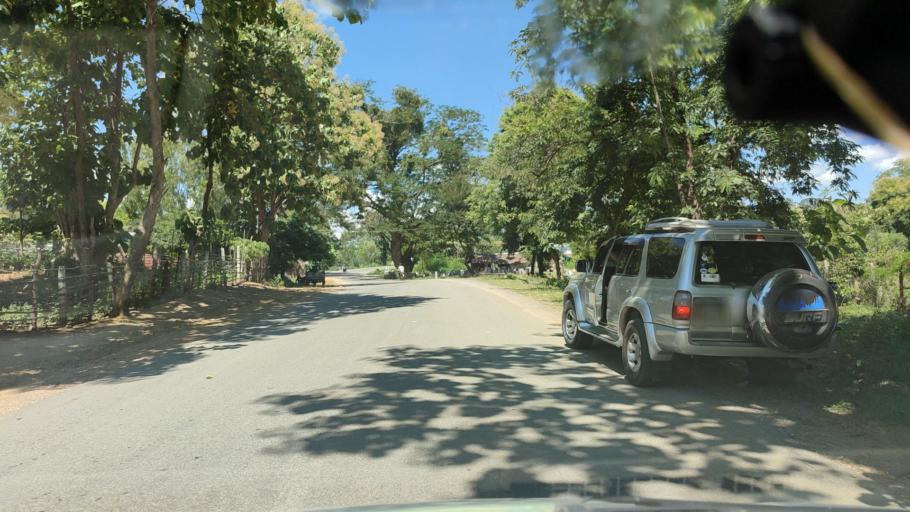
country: MM
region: Magway
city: Thayetmyo
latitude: 19.3406
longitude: 95.1604
